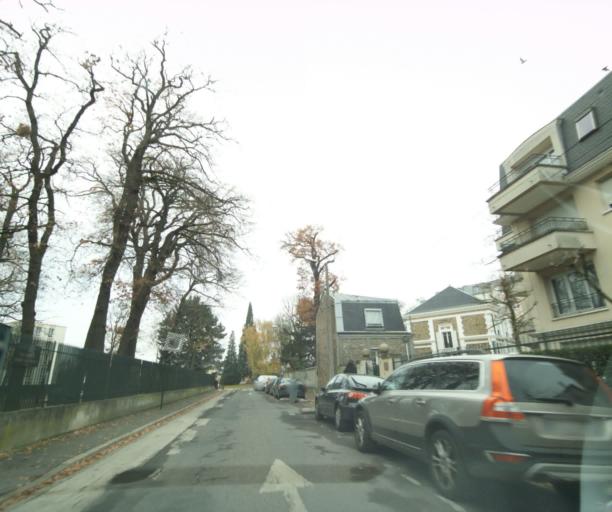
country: FR
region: Ile-de-France
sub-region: Departement de Seine-Saint-Denis
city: Livry-Gargan
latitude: 48.9257
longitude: 2.5403
